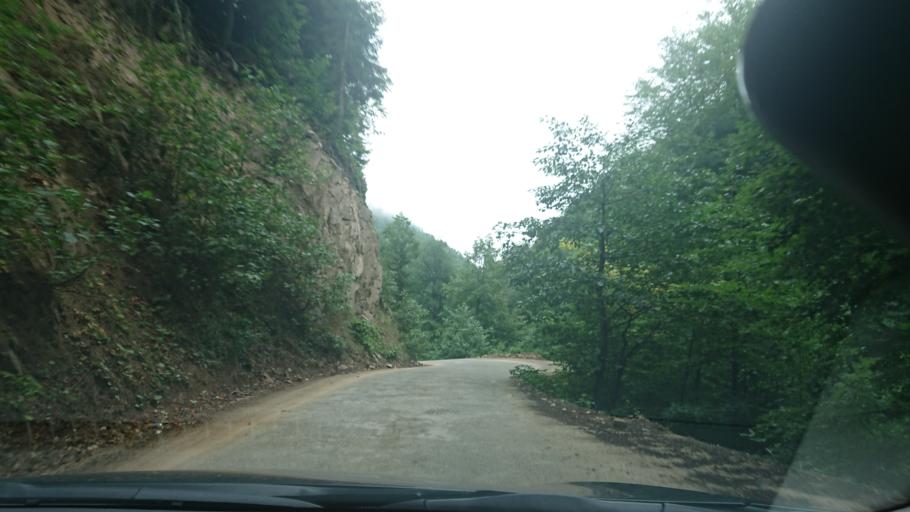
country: TR
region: Gumushane
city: Kurtun
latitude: 40.6717
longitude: 39.0436
